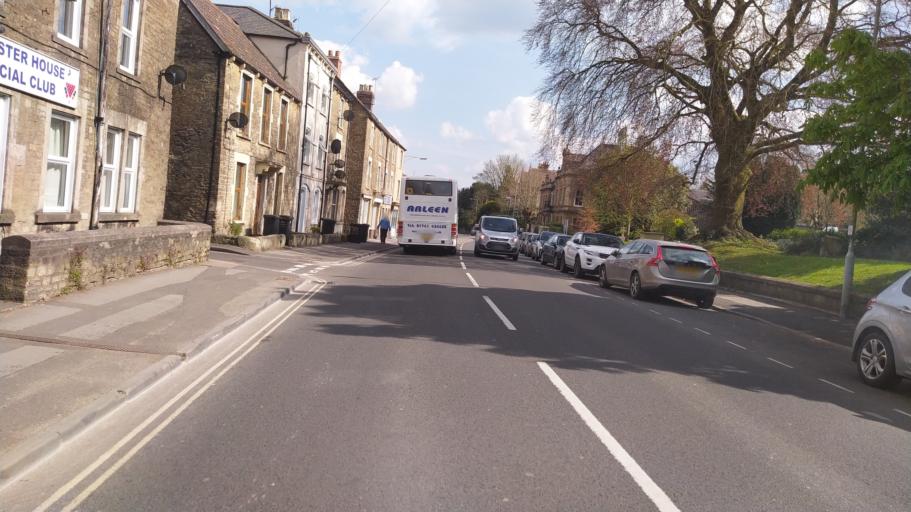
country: GB
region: England
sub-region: Somerset
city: Frome
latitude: 51.2301
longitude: -2.3259
